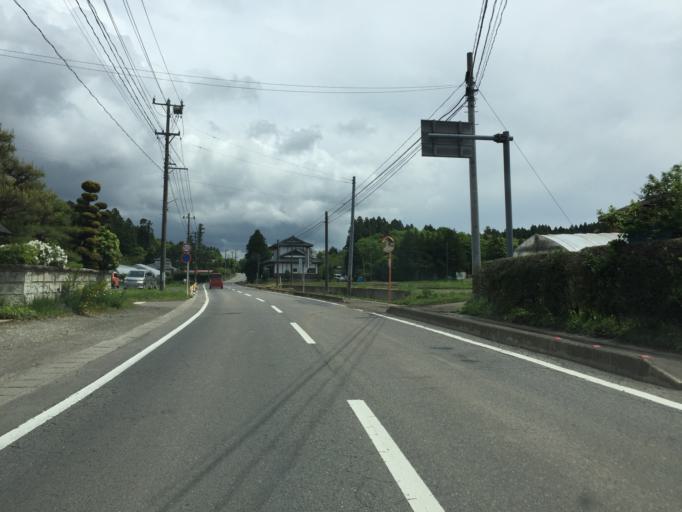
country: JP
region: Fukushima
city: Ishikawa
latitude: 37.1146
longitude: 140.3247
